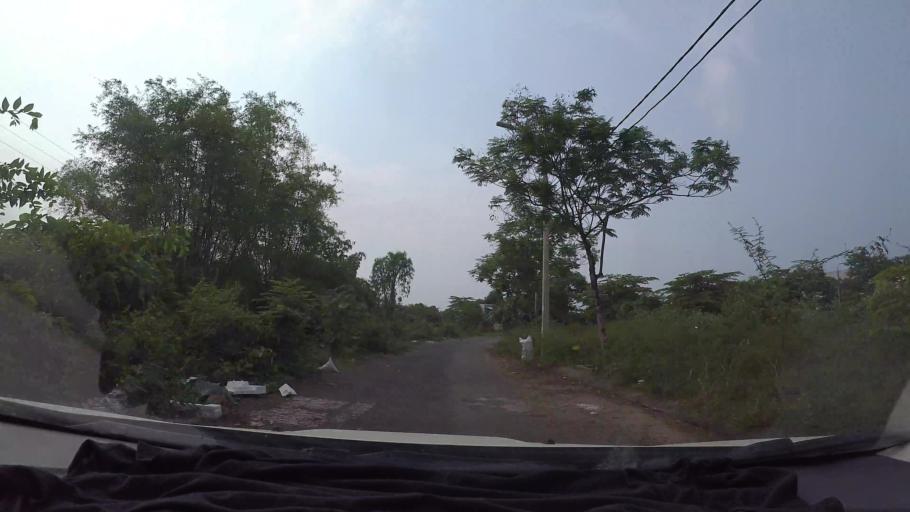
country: VN
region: Da Nang
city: Lien Chieu
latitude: 16.0573
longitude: 108.1593
